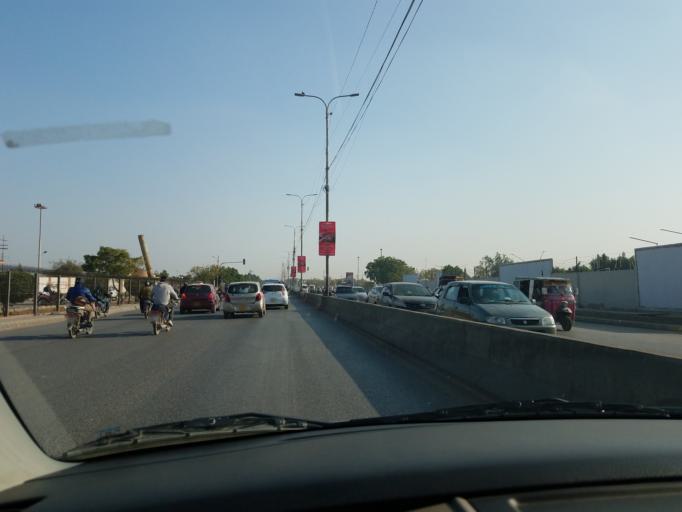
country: PK
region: Sindh
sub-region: Karachi District
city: Karachi
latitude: 24.8931
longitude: 67.1211
